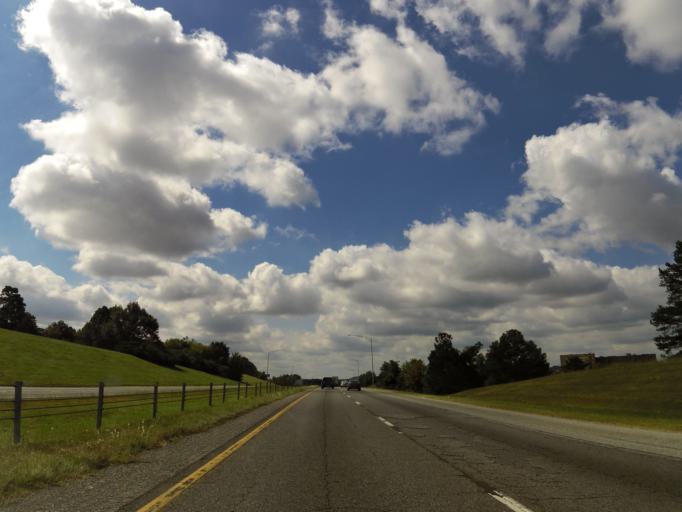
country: US
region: Alabama
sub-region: Jefferson County
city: Bessemer
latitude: 33.3734
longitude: -86.9956
